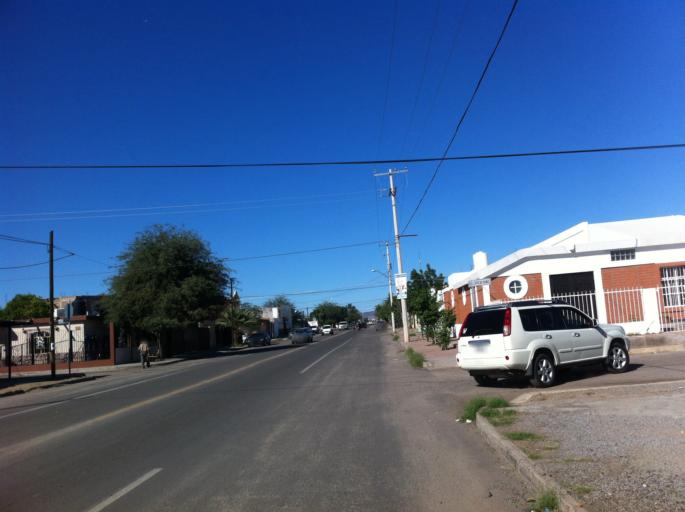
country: MX
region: Sonora
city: Hermosillo
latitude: 29.1044
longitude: -111.0055
